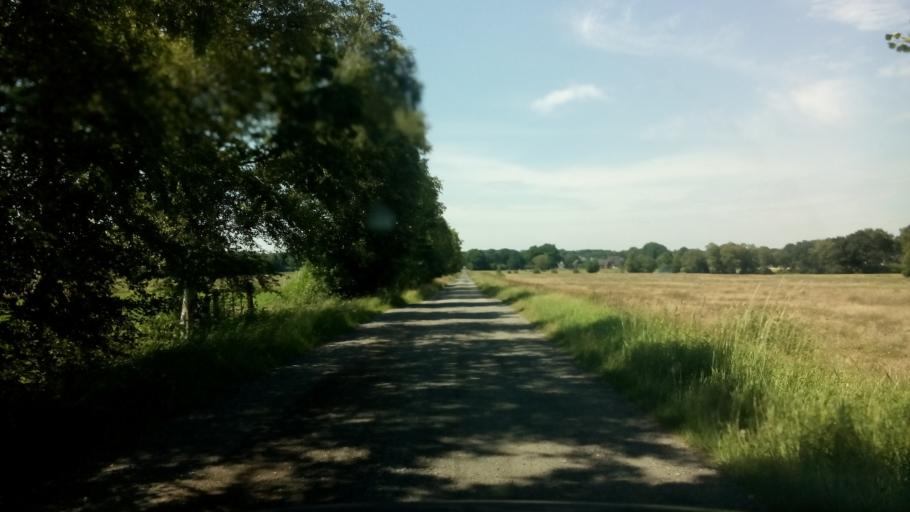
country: DE
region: Lower Saxony
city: Hambergen
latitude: 53.2663
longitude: 8.8334
